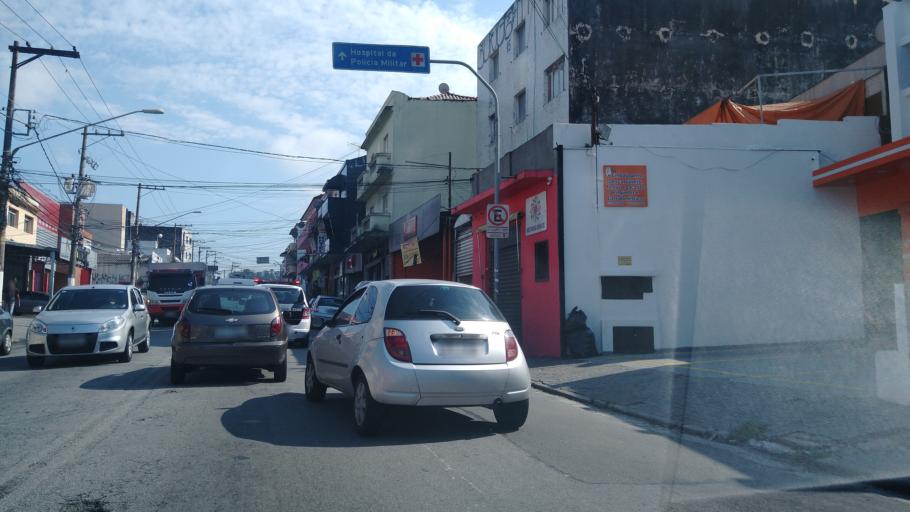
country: BR
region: Sao Paulo
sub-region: Sao Paulo
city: Sao Paulo
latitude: -23.4813
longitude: -46.6219
